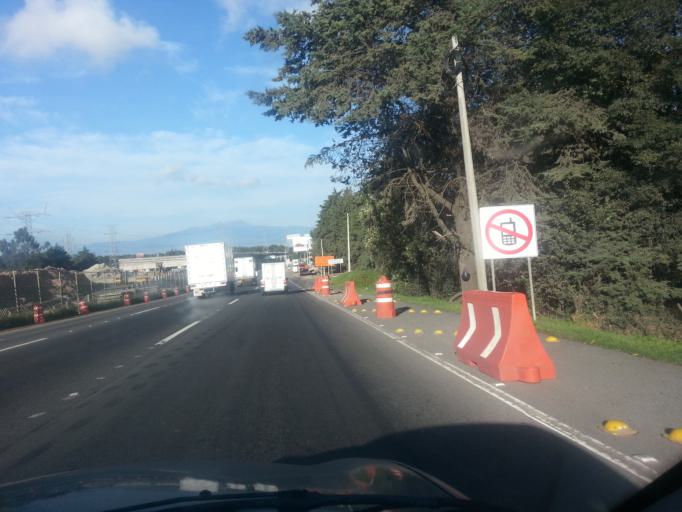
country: MX
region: Mexico
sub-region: Lerma
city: San Miguel Ameyalco
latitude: 19.2906
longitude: -99.4351
